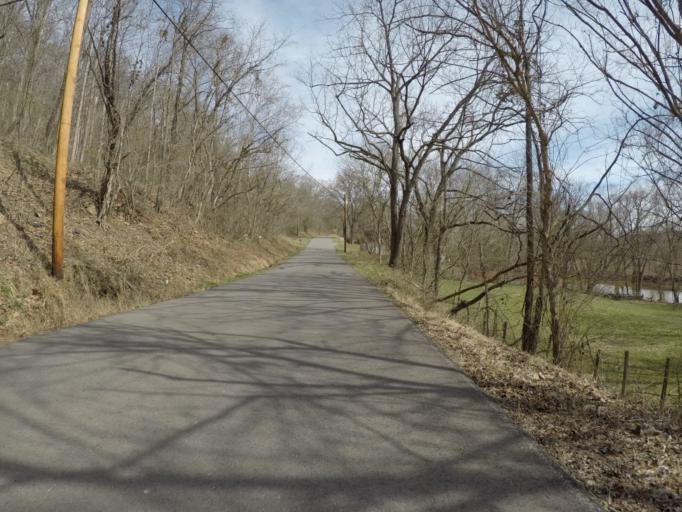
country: US
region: West Virginia
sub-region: Wayne County
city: Ceredo
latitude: 38.3733
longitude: -82.5493
